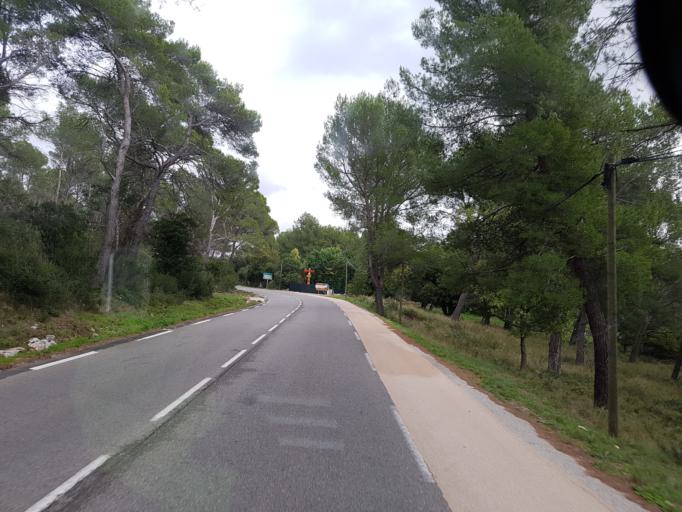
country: FR
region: Provence-Alpes-Cote d'Azur
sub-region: Departement des Bouches-du-Rhone
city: Cuges-les-Pins
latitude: 43.2685
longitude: 5.7204
